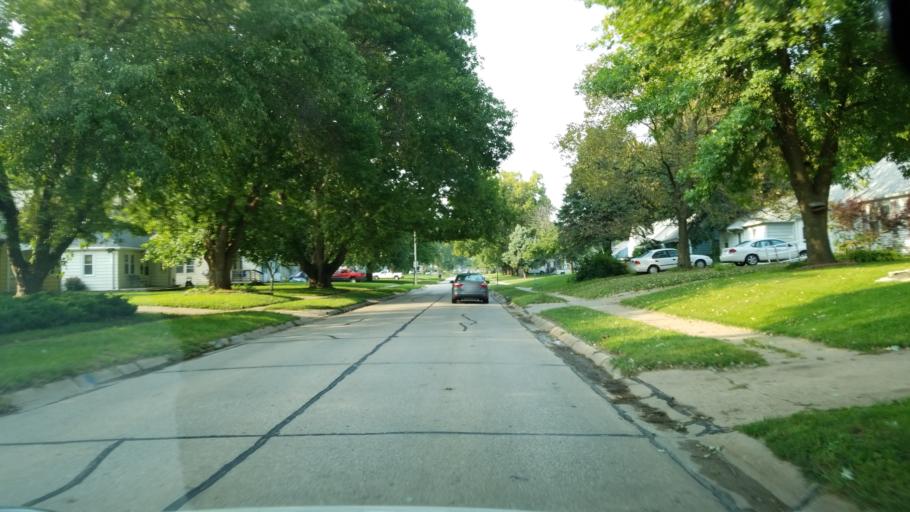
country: US
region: Nebraska
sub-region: Sarpy County
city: Bellevue
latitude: 41.1314
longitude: -95.8924
